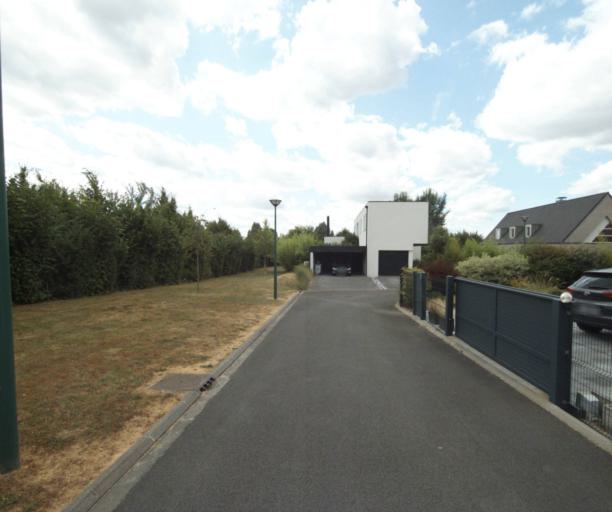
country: FR
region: Nord-Pas-de-Calais
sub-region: Departement du Nord
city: Wasquehal
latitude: 50.6843
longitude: 3.1273
